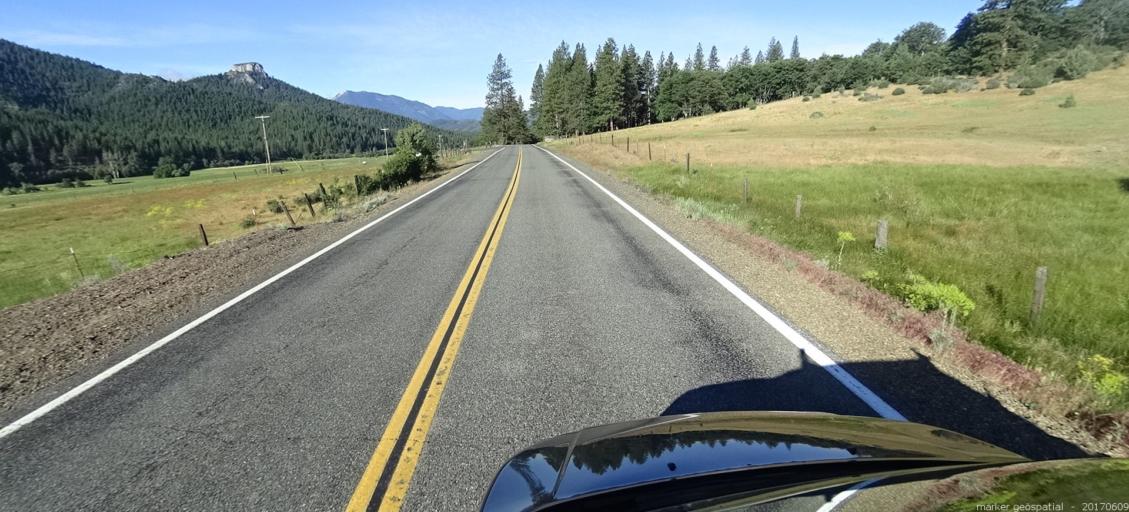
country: US
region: California
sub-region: Siskiyou County
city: Weed
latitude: 41.3879
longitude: -122.6787
